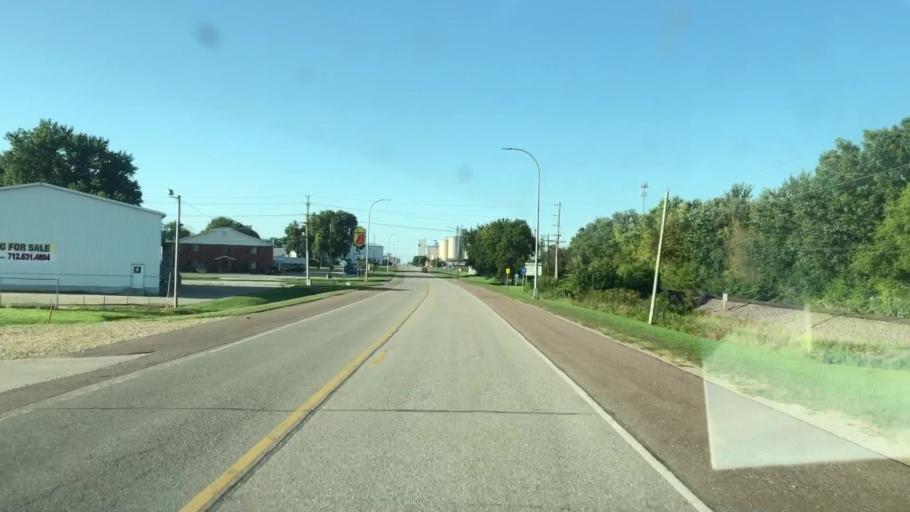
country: US
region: Iowa
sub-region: O'Brien County
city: Sheldon
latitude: 43.1906
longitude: -95.8522
